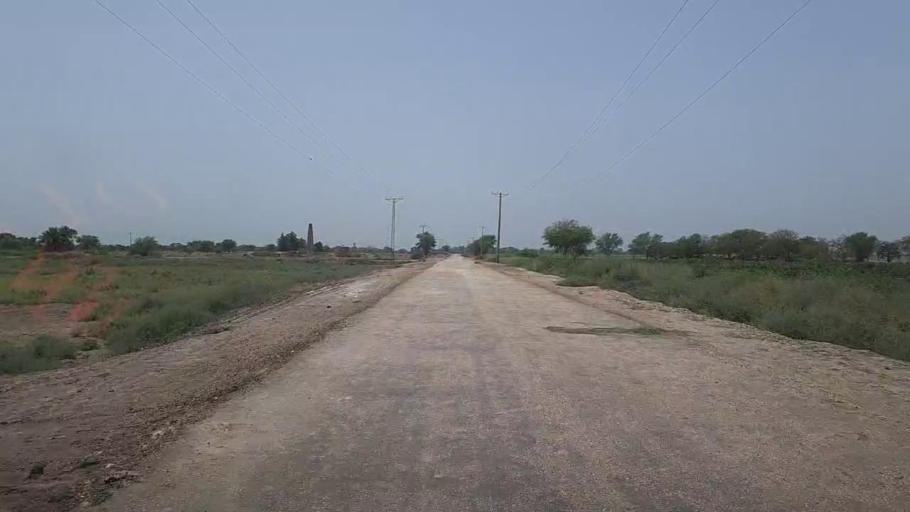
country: PK
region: Sindh
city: Pad Idan
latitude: 26.8343
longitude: 68.3178
